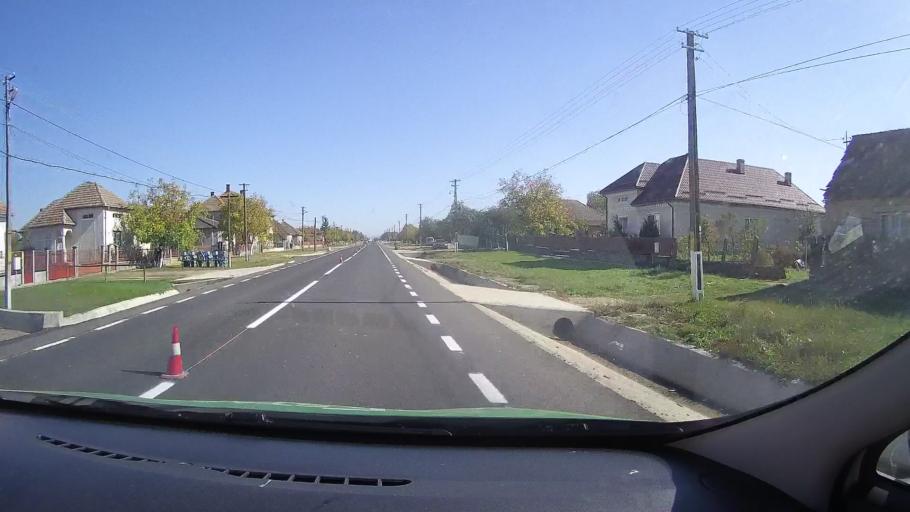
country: RO
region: Satu Mare
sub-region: Oras Ardud
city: Madaras
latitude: 47.6837
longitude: 22.8630
